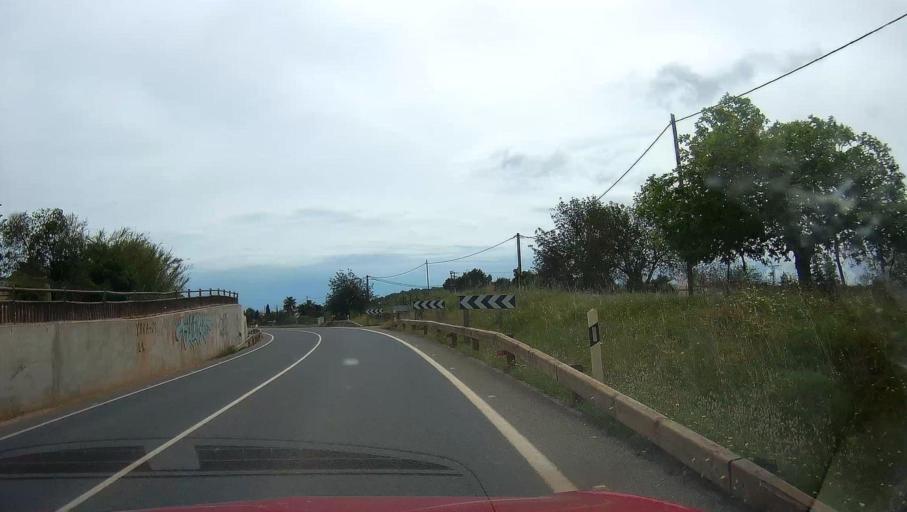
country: ES
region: Balearic Islands
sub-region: Illes Balears
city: Sant Joan de Labritja
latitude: 39.0164
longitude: 1.4270
